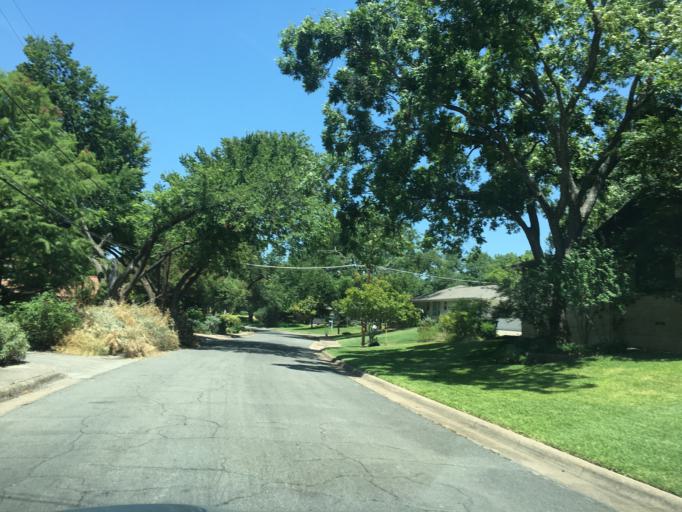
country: US
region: Texas
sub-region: Dallas County
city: Highland Park
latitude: 32.8359
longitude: -96.7390
